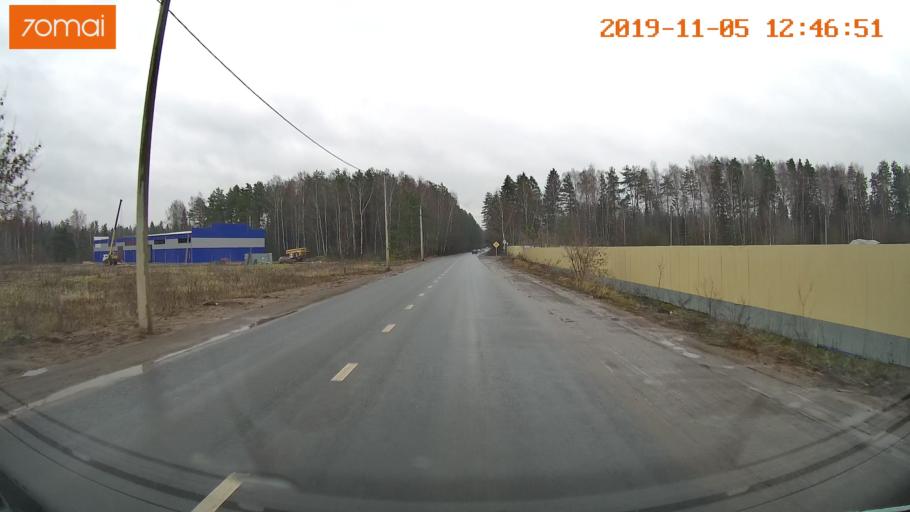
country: RU
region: Ivanovo
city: Kokhma
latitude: 56.9714
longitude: 41.0802
